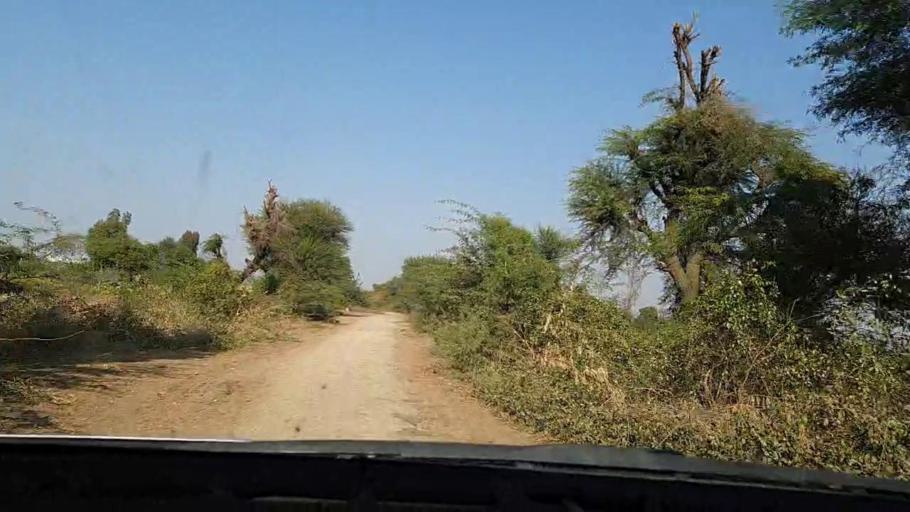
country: PK
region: Sindh
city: Tando Mittha Khan
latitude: 25.8094
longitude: 69.3277
